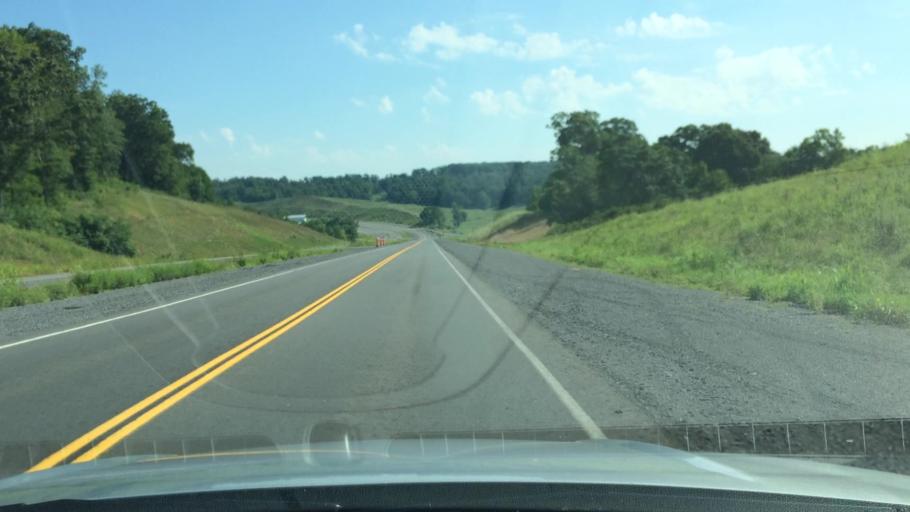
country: US
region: Tennessee
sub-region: Jefferson County
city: White Pine
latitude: 36.1189
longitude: -83.3382
